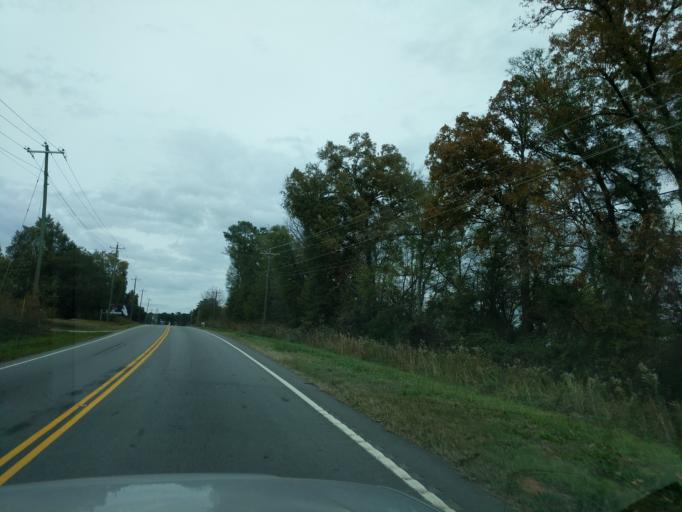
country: US
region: South Carolina
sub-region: Newberry County
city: Newberry
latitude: 34.2439
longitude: -81.6454
